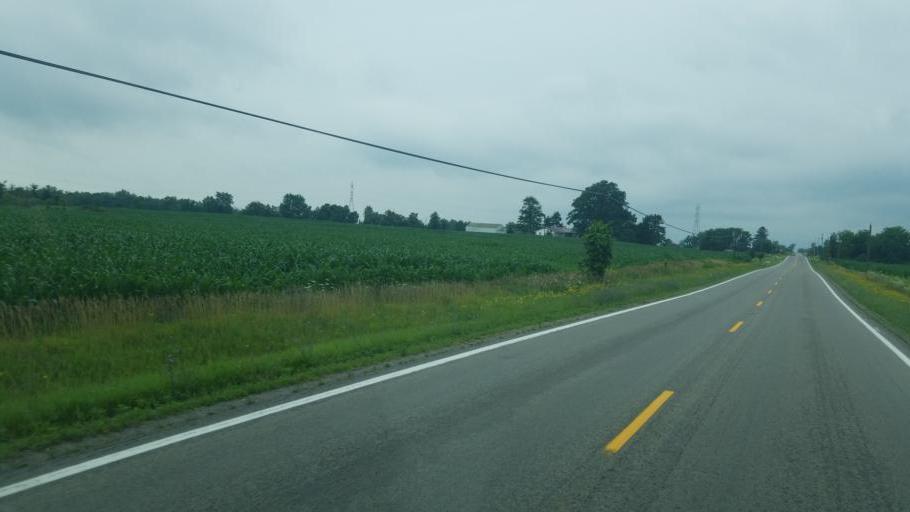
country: US
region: Ohio
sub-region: Logan County
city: Northwood
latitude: 40.5994
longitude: -83.7380
